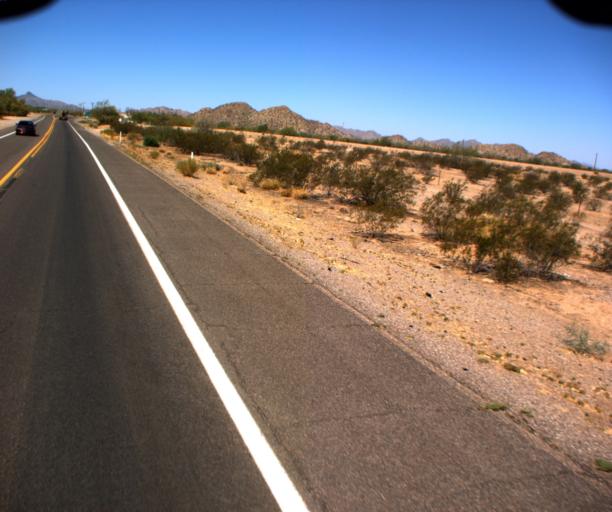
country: US
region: Arizona
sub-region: Pinal County
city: Maricopa
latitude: 32.8770
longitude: -112.0456
